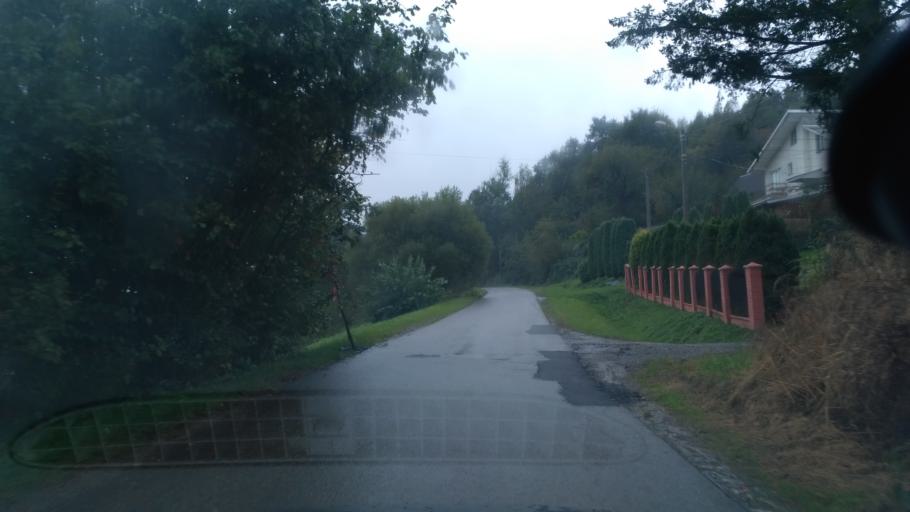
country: PL
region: Subcarpathian Voivodeship
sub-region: Powiat ropczycko-sedziszowski
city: Niedzwiada
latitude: 50.0115
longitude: 21.5479
